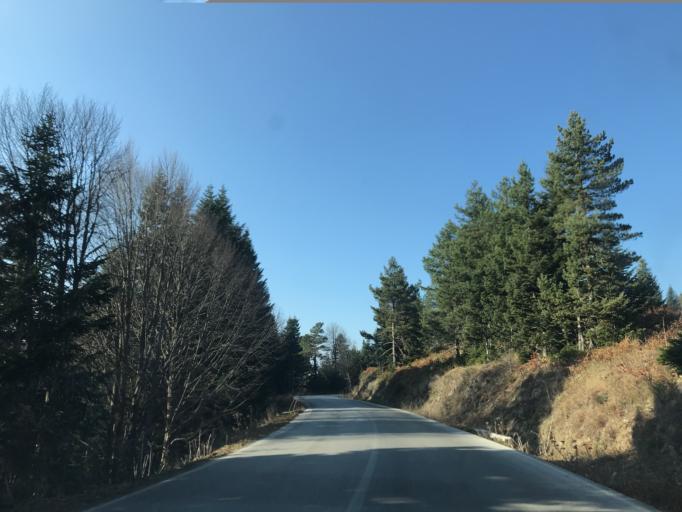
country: TR
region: Bolu
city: Bolu
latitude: 40.8887
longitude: 31.6777
